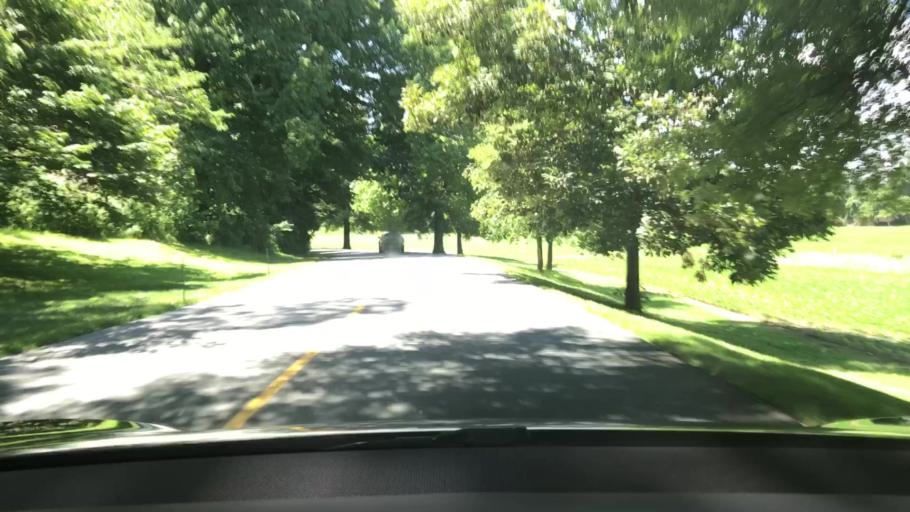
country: US
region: North Carolina
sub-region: Buncombe County
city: Asheville
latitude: 35.5644
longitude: -82.5693
